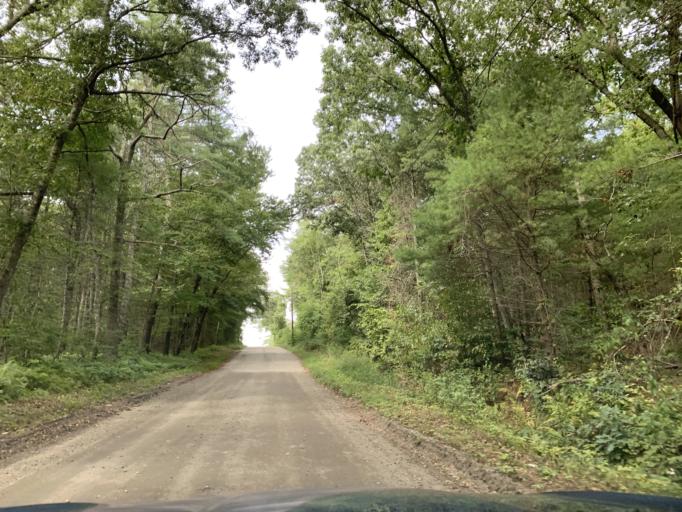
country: US
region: Rhode Island
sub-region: Kent County
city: West Greenwich
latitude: 41.5782
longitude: -71.6517
